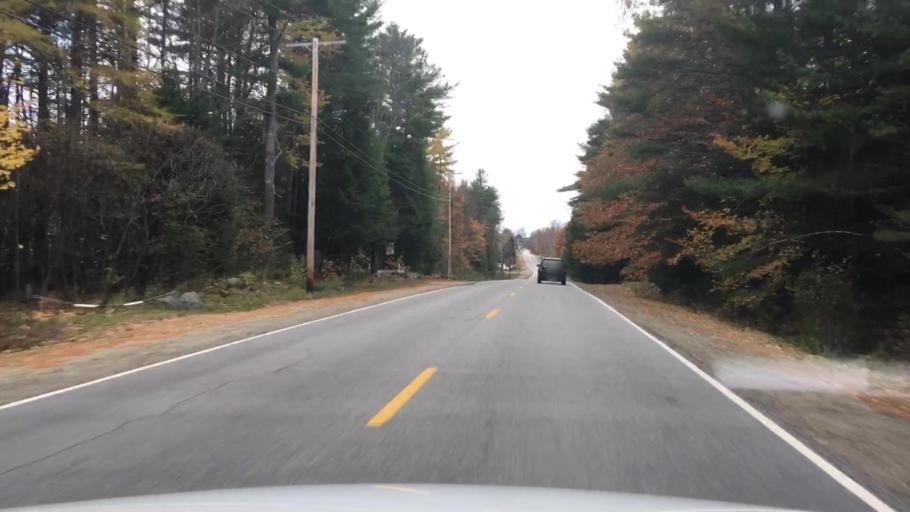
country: US
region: Maine
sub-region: Kennebec County
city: Monmouth
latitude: 44.1899
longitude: -70.0686
